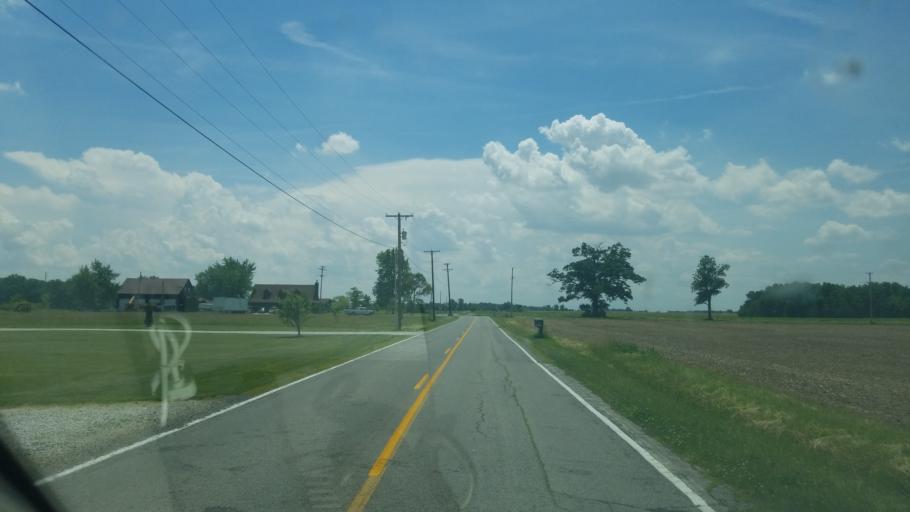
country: US
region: Ohio
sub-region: Hancock County
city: Arlington
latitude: 40.9080
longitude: -83.5948
